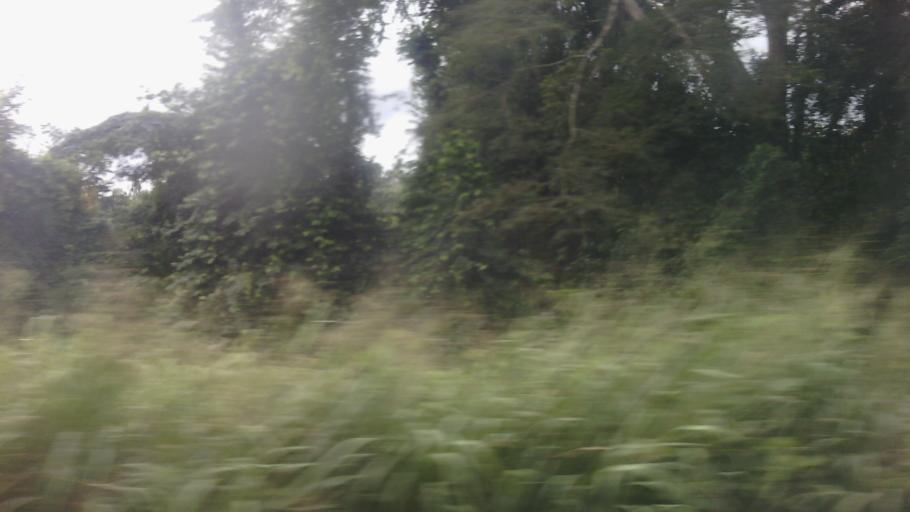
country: CI
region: Sud-Comoe
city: Aboisso
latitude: 5.4165
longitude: -3.2787
